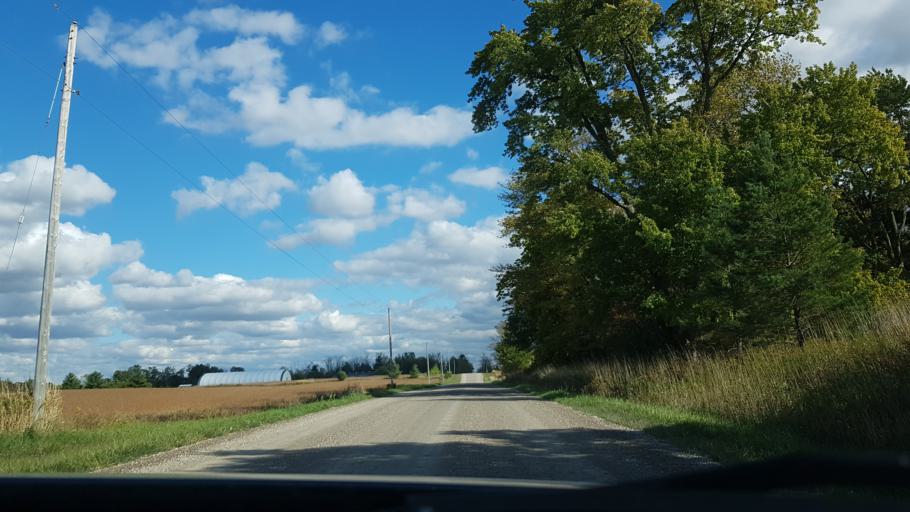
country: CA
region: Ontario
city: South Huron
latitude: 43.1121
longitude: -81.6446
